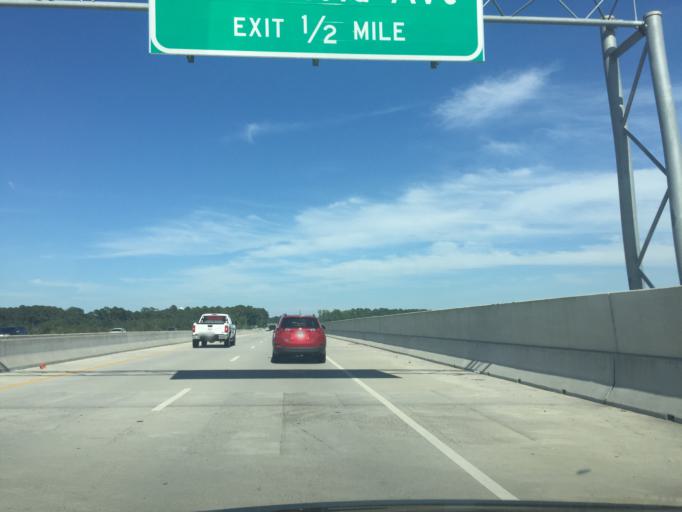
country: US
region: Georgia
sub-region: Chatham County
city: Montgomery
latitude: 31.9752
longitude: -81.1194
